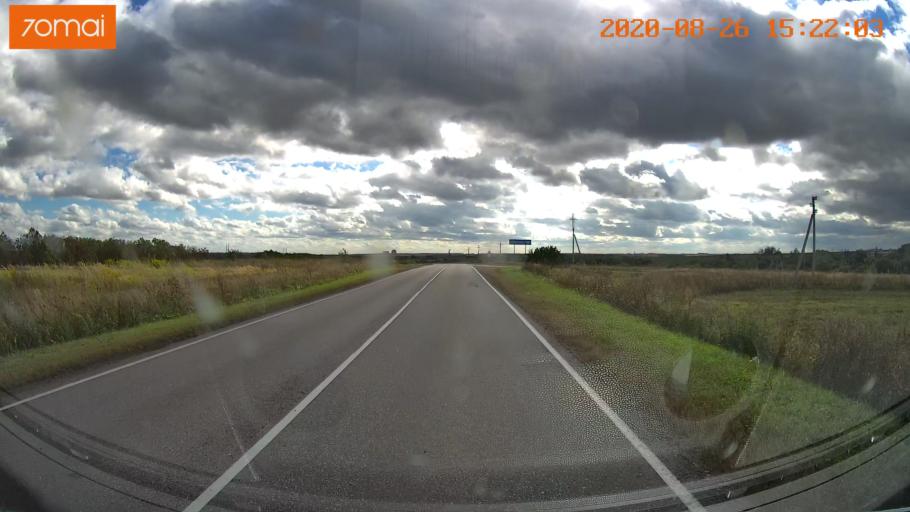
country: RU
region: Tula
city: Severo-Zadonsk
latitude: 54.1370
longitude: 38.4566
